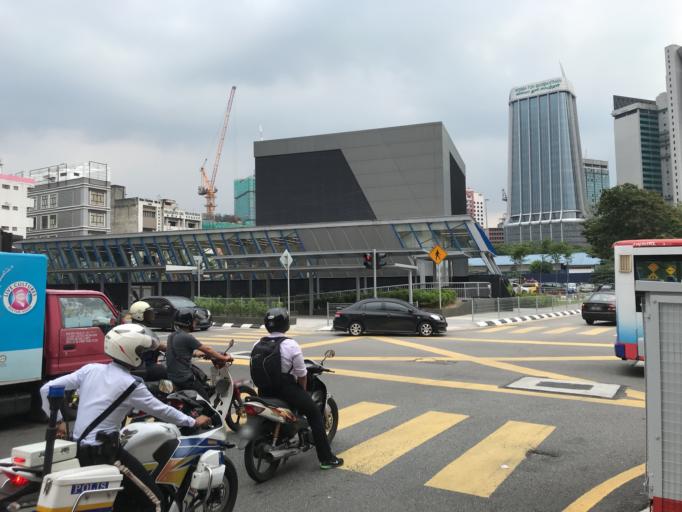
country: MY
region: Kuala Lumpur
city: Kuala Lumpur
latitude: 3.1428
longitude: 101.6965
